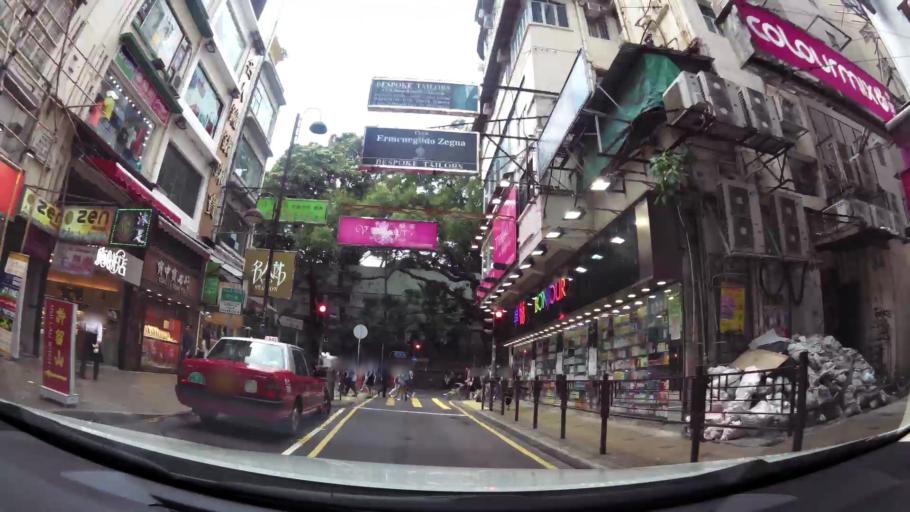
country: HK
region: Wanchai
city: Wan Chai
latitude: 22.2975
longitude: 114.1711
